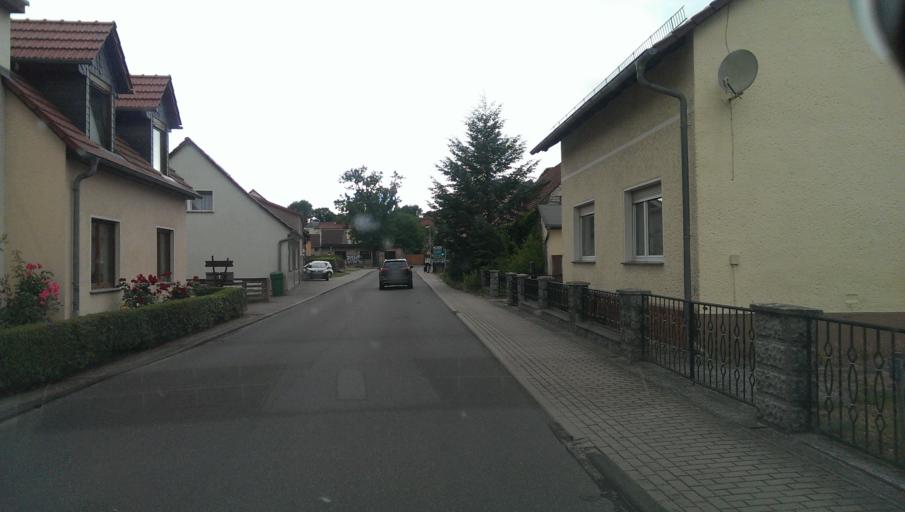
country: DE
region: Brandenburg
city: Gross Kreutz
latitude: 52.3183
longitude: 12.7473
